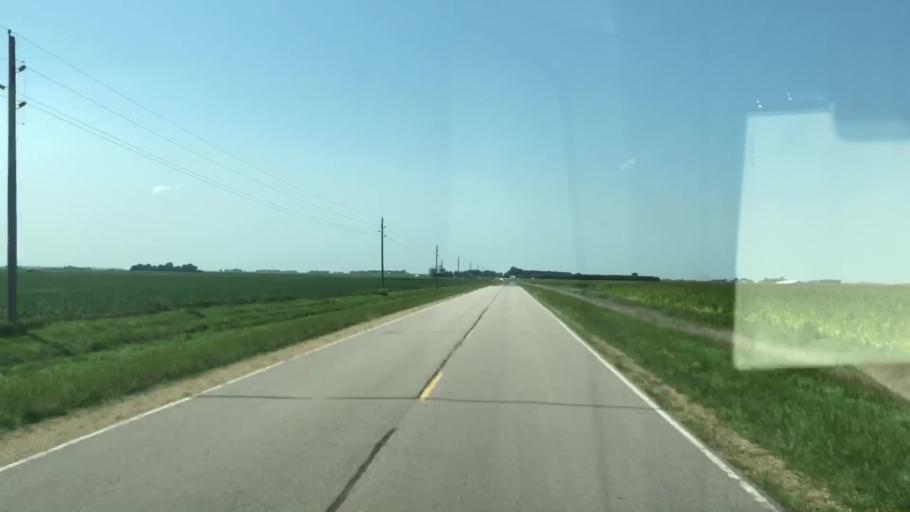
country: US
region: Iowa
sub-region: O'Brien County
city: Sheldon
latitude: 43.2443
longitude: -95.7951
